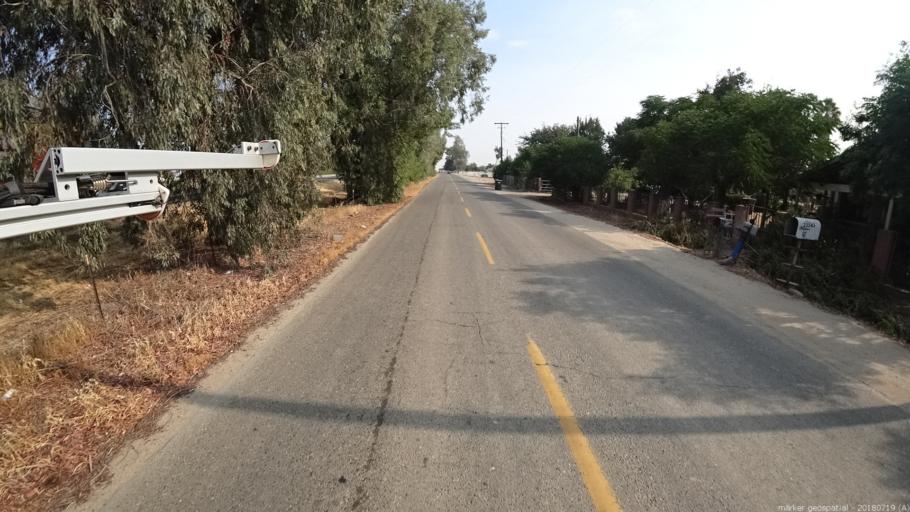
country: US
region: California
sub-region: Madera County
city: Fairmead
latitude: 37.0919
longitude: -120.2132
